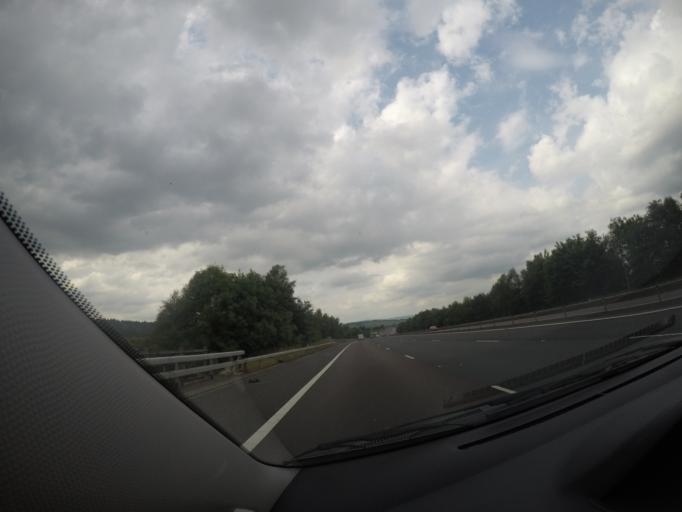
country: GB
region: Scotland
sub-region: Dumfries and Galloway
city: Moffat
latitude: 55.2923
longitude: -3.4397
